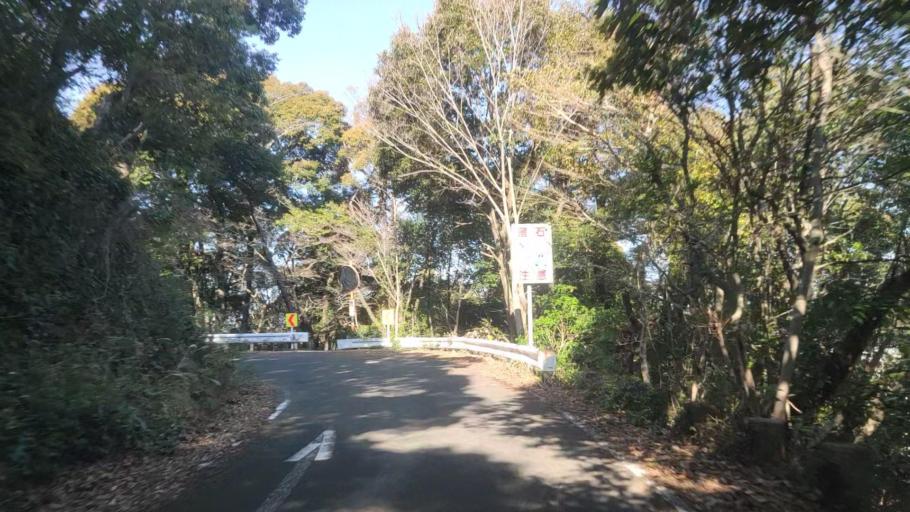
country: JP
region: Gifu
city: Gifu-shi
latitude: 35.4303
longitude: 136.7708
